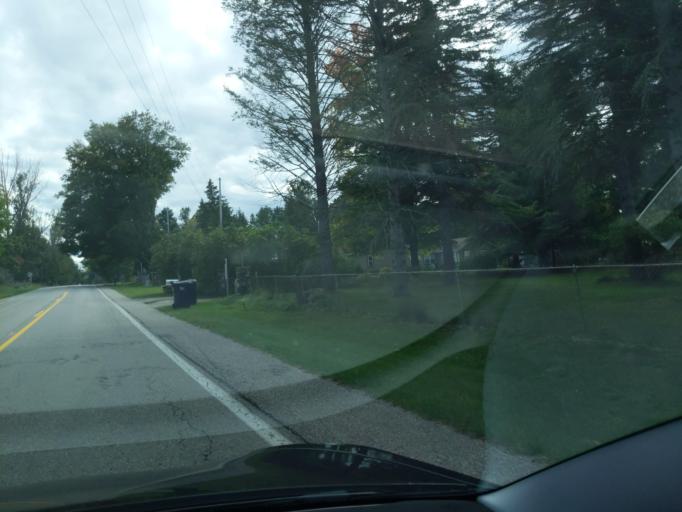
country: US
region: Michigan
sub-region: Kalkaska County
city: Rapid City
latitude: 44.9241
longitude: -85.2857
